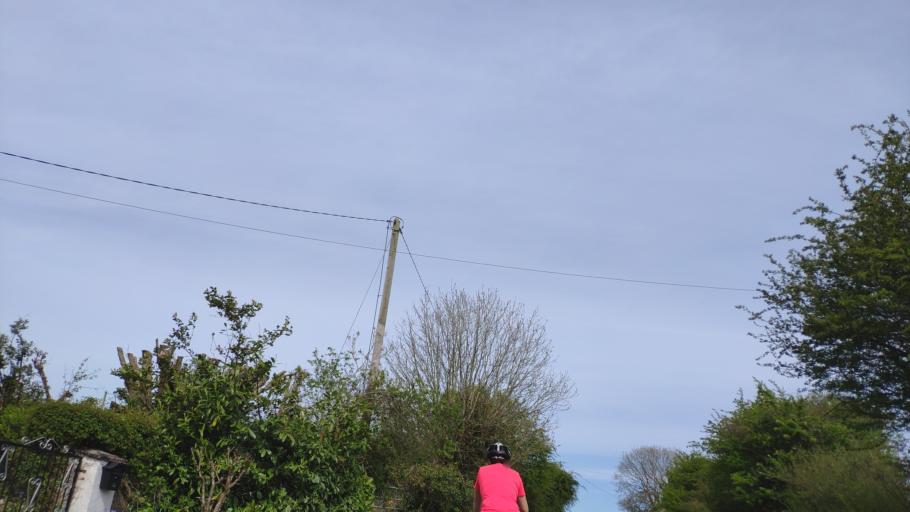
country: IE
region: Munster
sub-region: County Cork
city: Blarney
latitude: 51.9589
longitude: -8.5114
